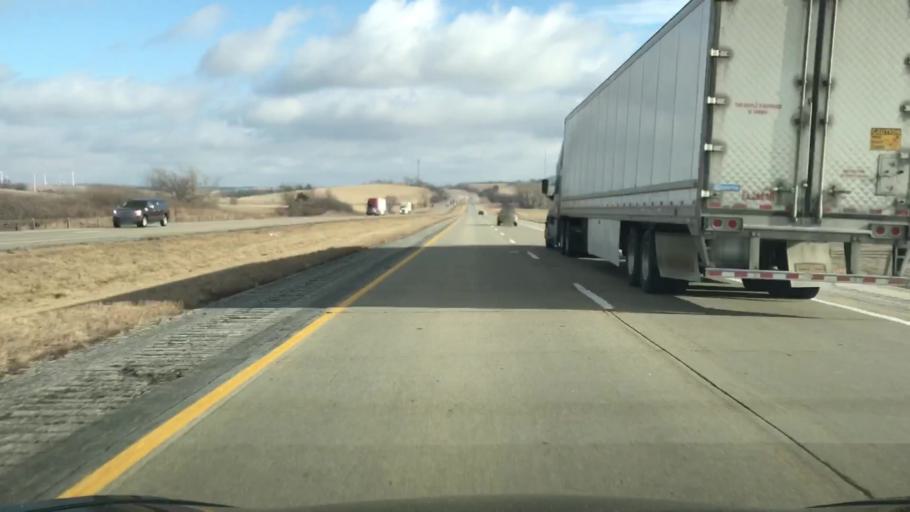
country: US
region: Iowa
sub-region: Cass County
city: Atlantic
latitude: 41.4967
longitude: -94.8014
